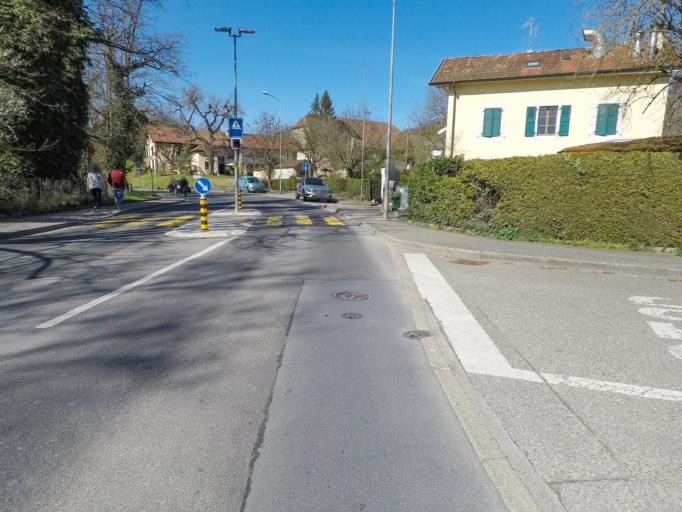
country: CH
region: Geneva
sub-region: Geneva
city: Aire-la-Ville
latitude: 46.2002
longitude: 6.0444
